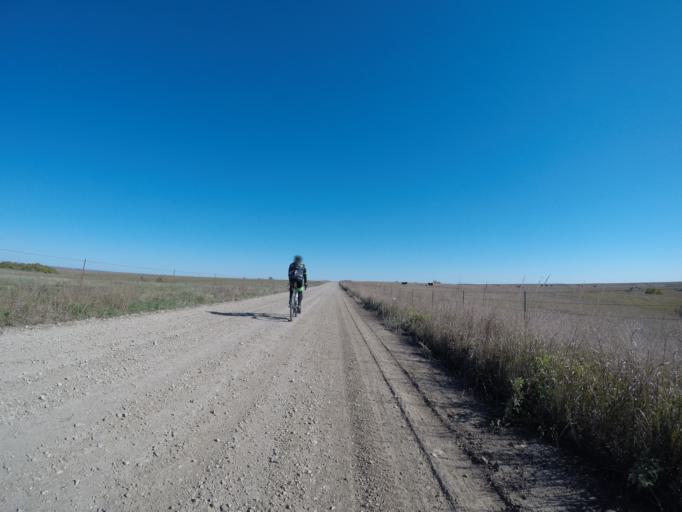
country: US
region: Kansas
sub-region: Wabaunsee County
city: Alma
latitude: 38.8820
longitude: -96.3662
